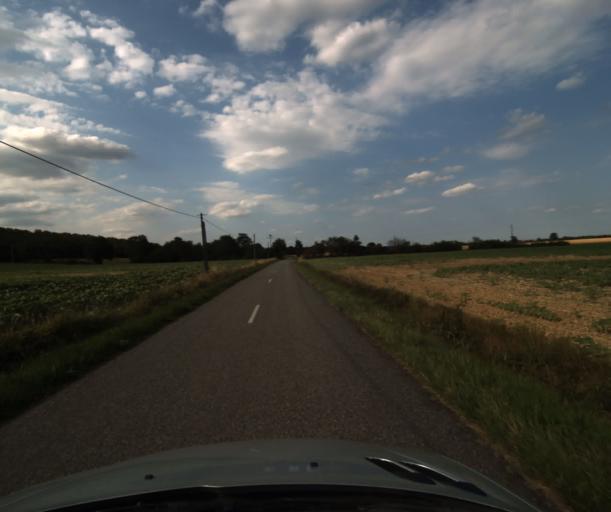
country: FR
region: Midi-Pyrenees
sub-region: Departement de la Haute-Garonne
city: Fonsorbes
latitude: 43.5231
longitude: 1.2315
